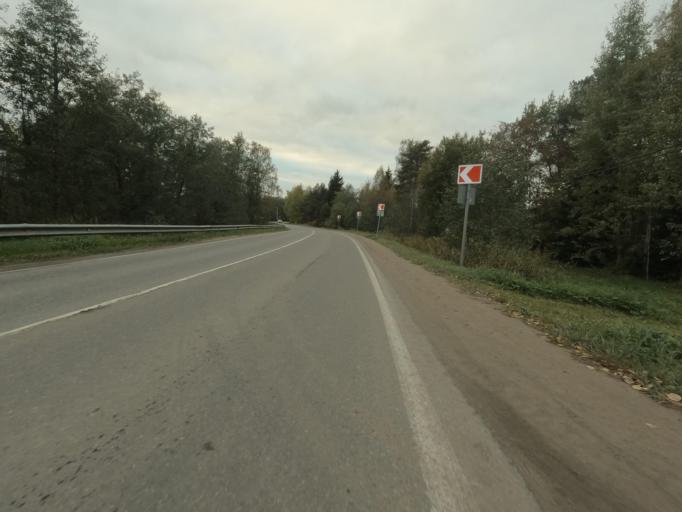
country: RU
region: Leningrad
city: Pavlovo
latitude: 59.7861
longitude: 30.9691
